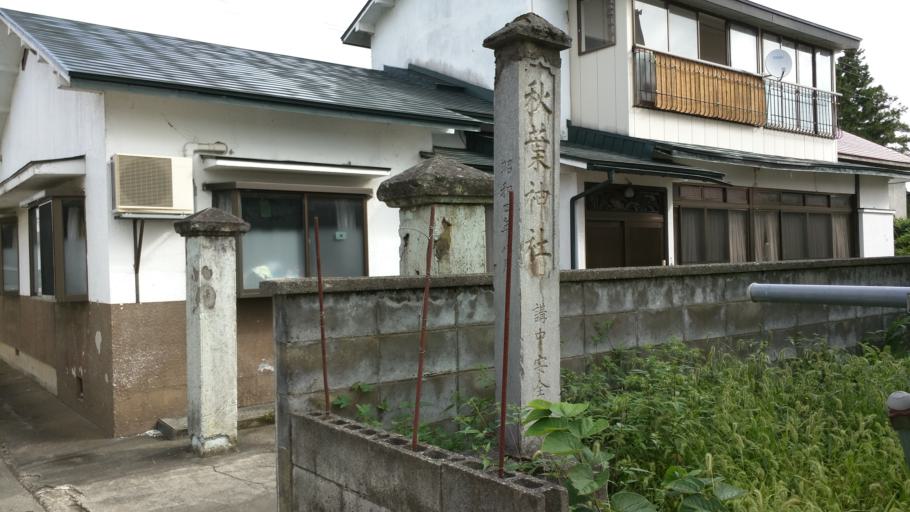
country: JP
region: Fukushima
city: Kitakata
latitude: 37.5458
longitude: 139.8078
